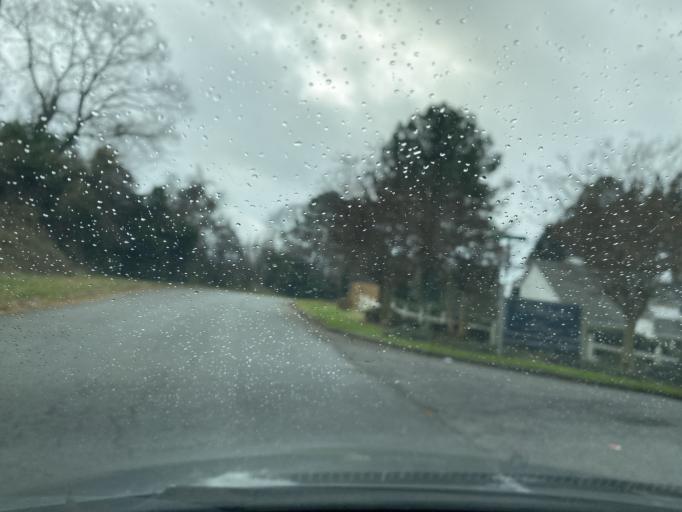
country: US
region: Georgia
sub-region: DeKalb County
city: Pine Mountain
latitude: 33.6992
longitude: -84.1467
